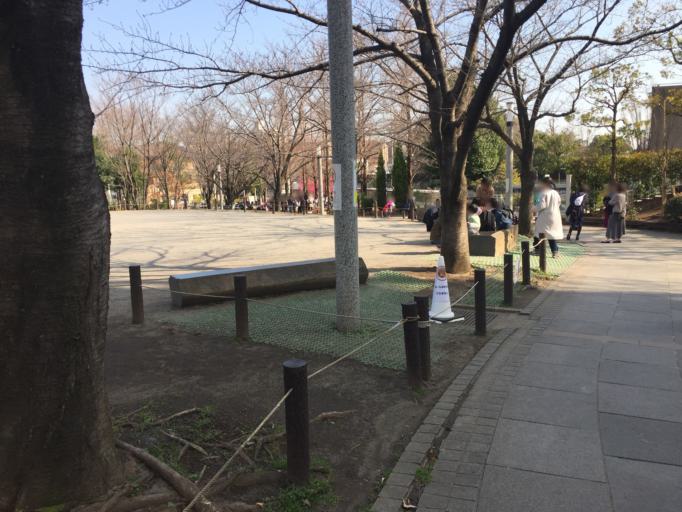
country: JP
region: Tokyo
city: Tokyo
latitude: 35.6211
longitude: 139.6734
